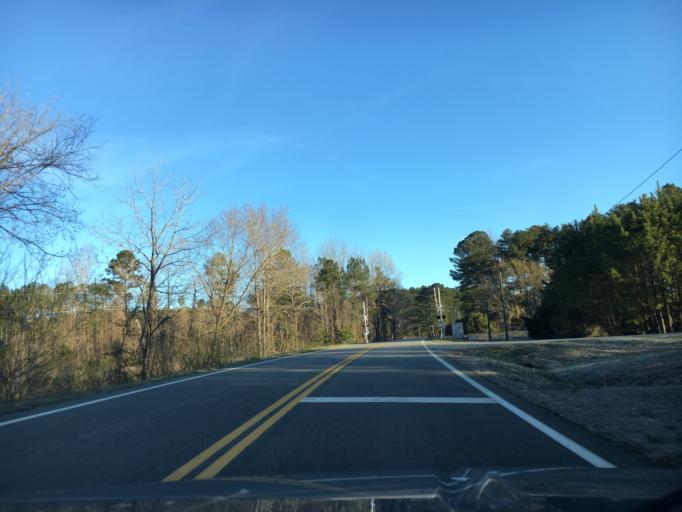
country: US
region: Virginia
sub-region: Halifax County
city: Halifax
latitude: 36.7646
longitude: -78.9158
